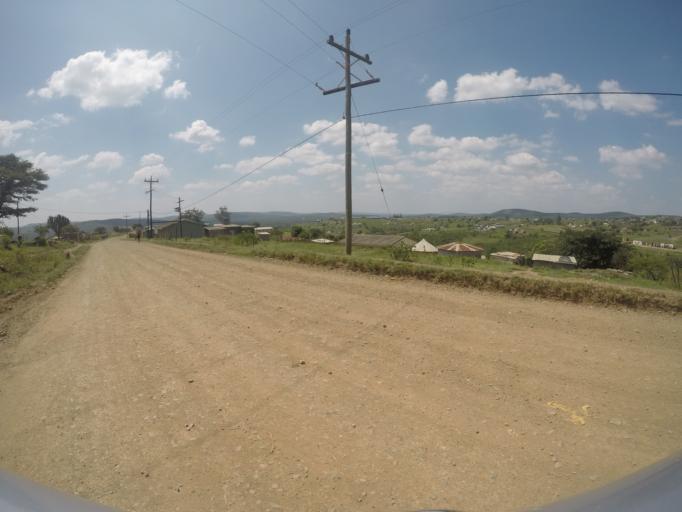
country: ZA
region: KwaZulu-Natal
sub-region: uThungulu District Municipality
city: Empangeni
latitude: -28.5984
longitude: 31.7420
